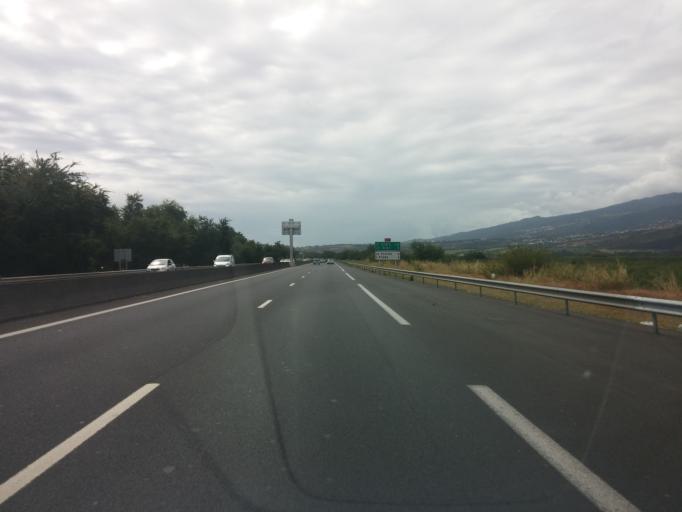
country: RE
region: Reunion
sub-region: Reunion
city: Saint-Paul
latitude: -21.0034
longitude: 55.2818
